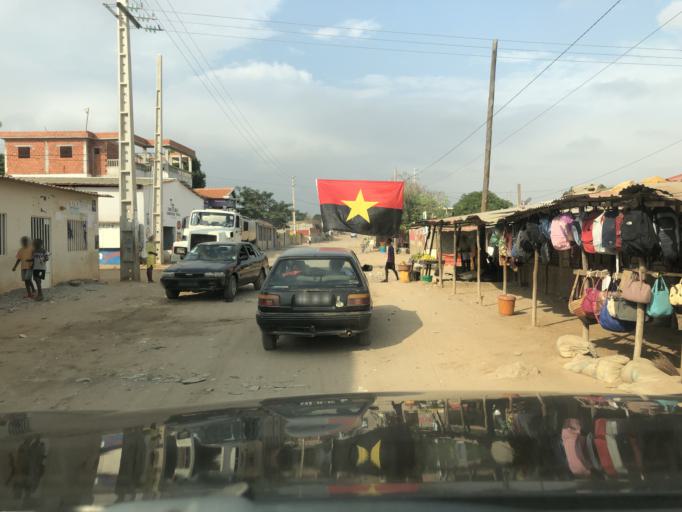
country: AO
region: Luanda
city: Luanda
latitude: -8.9343
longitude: 13.2317
